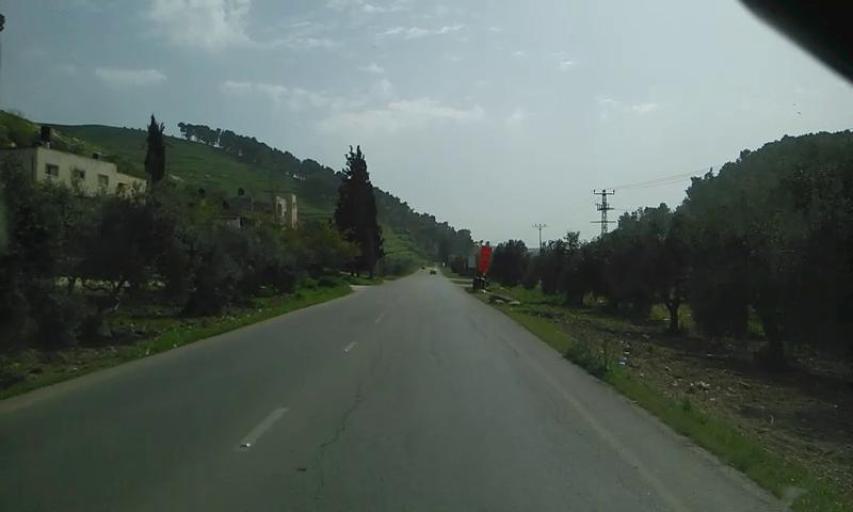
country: PS
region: West Bank
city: Mirkah
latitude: 32.4043
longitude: 35.2261
